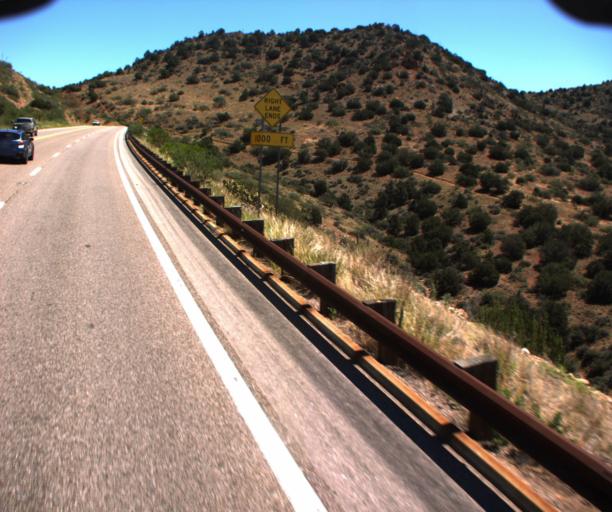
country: US
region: Arizona
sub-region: Gila County
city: Globe
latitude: 33.5076
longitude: -110.7044
